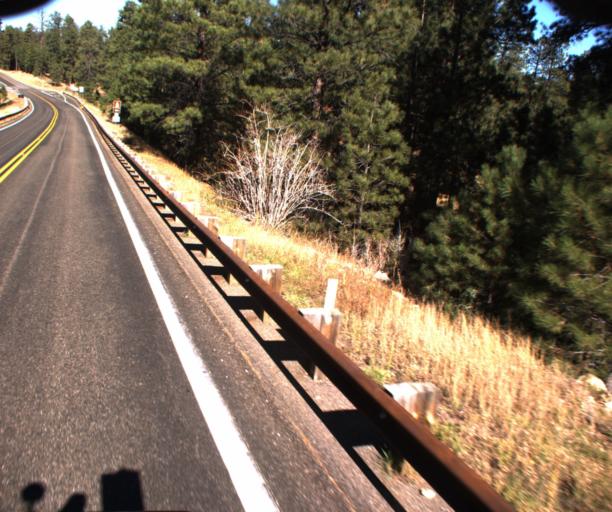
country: US
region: Arizona
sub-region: Coconino County
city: Fredonia
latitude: 36.7074
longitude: -112.2187
